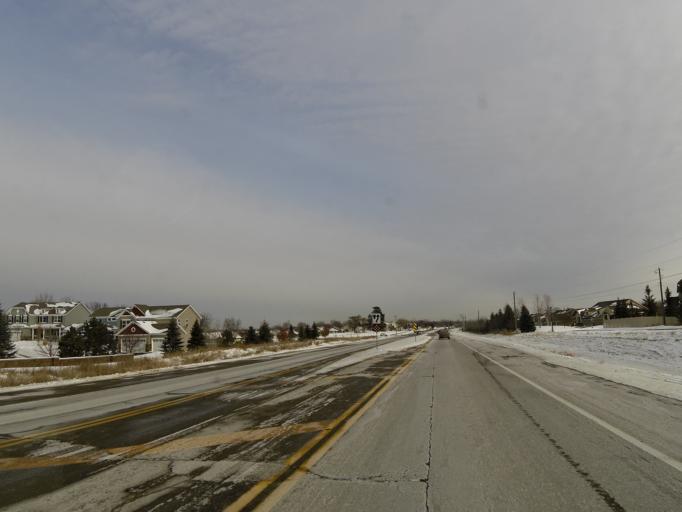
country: US
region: Minnesota
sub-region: Scott County
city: Prior Lake
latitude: 44.7012
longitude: -93.4459
